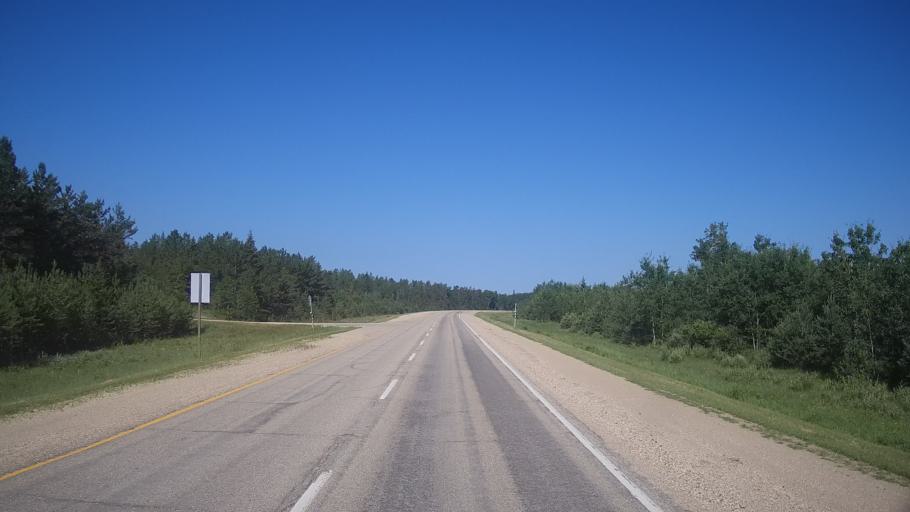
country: CA
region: Manitoba
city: La Broquerie
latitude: 49.6494
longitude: -95.9683
